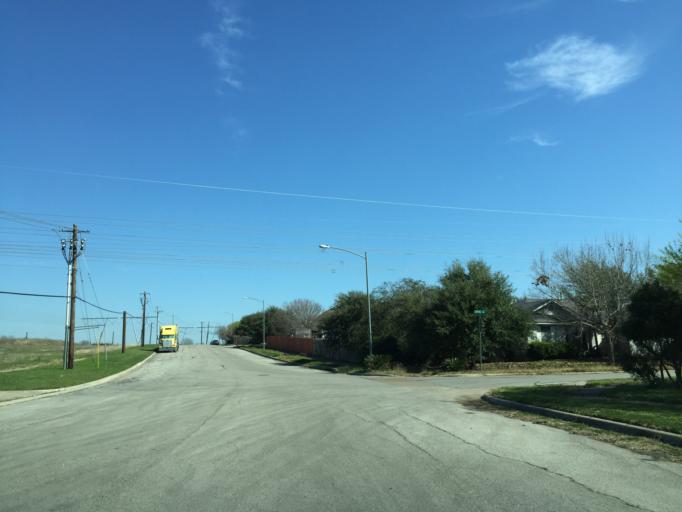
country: US
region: Texas
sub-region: Travis County
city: Garfield
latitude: 30.1593
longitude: -97.6515
